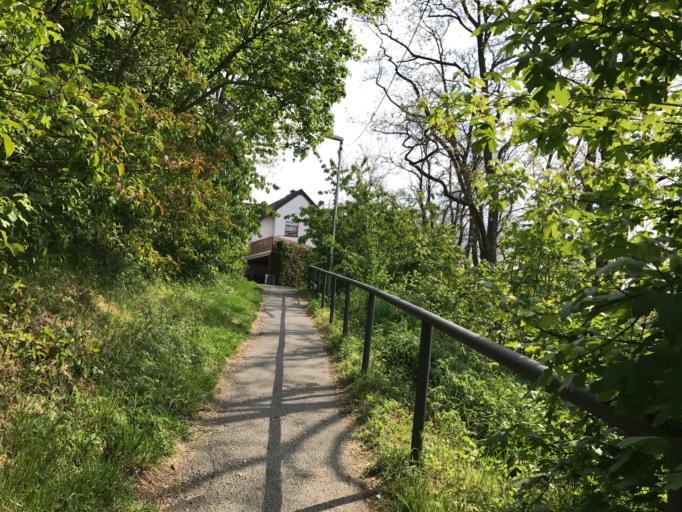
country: DE
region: Rheinland-Pfalz
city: Mainz
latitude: 49.9731
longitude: 8.2746
